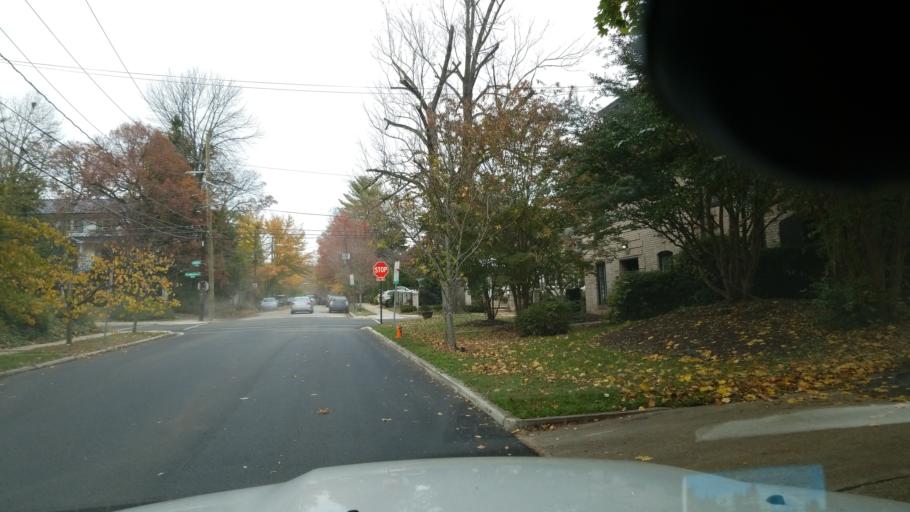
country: US
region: Maryland
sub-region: Montgomery County
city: Chevy Chase Village
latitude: 38.9493
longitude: -77.0616
